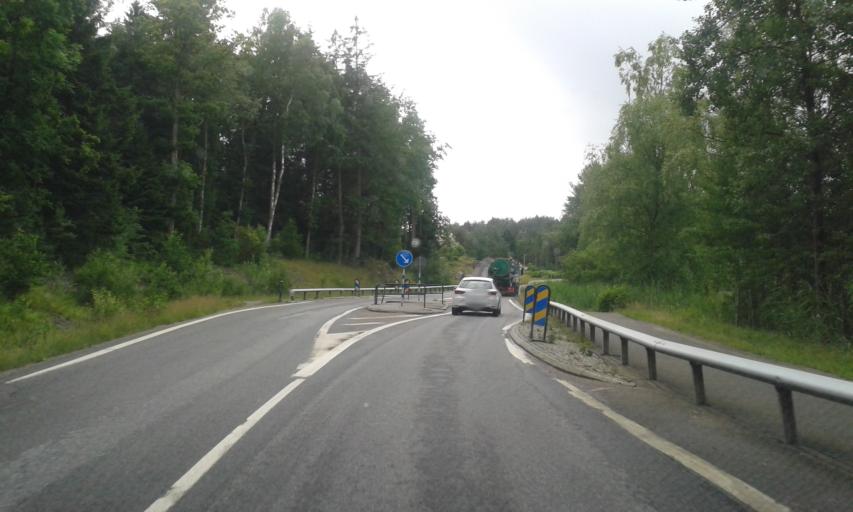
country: SE
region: Vaestra Goetaland
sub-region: Kungalvs Kommun
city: Diserod
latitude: 57.8974
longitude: 12.0050
